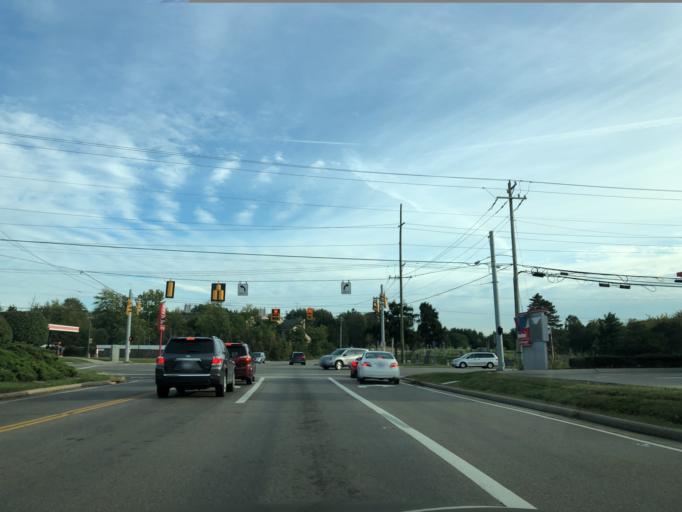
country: US
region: Ohio
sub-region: Hamilton County
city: Sixteen Mile Stand
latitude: 39.2883
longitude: -84.3052
